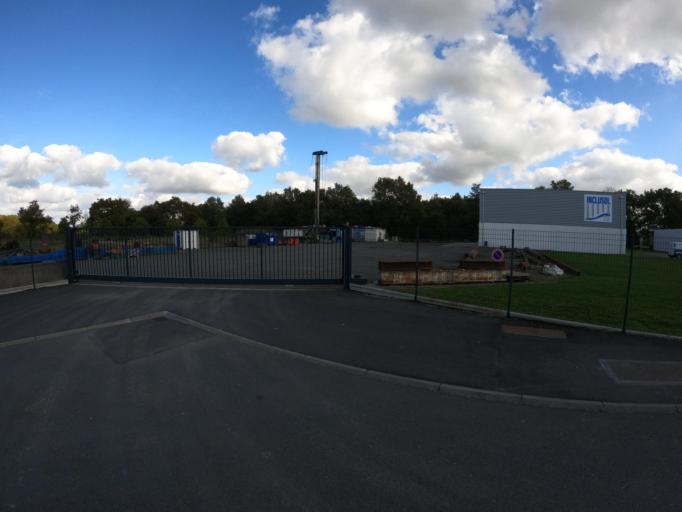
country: FR
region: Pays de la Loire
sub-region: Departement de la Loire-Atlantique
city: Le Bignon
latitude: 47.0999
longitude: -1.4489
